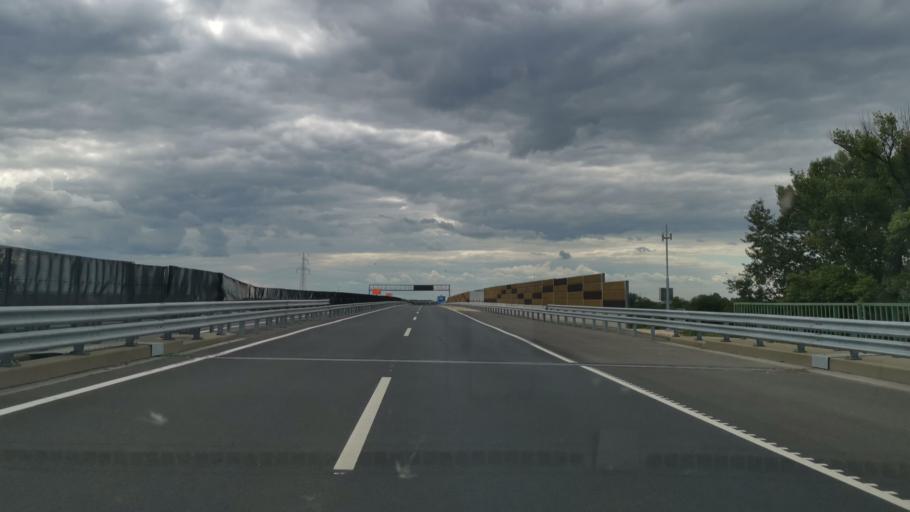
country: HU
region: Jasz-Nagykun-Szolnok
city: Zagyvarekas
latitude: 47.2187
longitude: 20.1528
